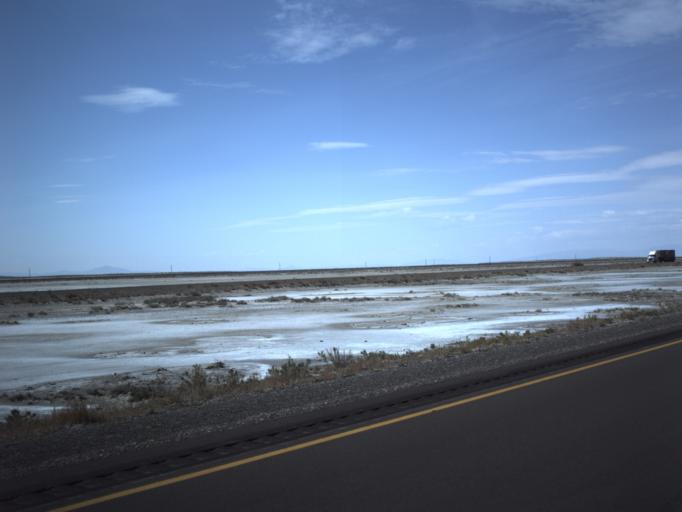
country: US
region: Utah
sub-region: Tooele County
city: Wendover
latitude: 40.7282
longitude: -113.3079
